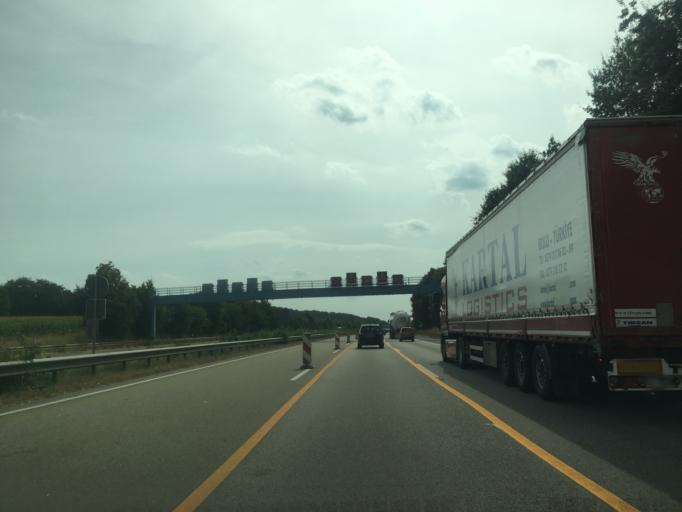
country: DE
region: Rheinland-Pfalz
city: Wehr
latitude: 50.4169
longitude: 7.2338
